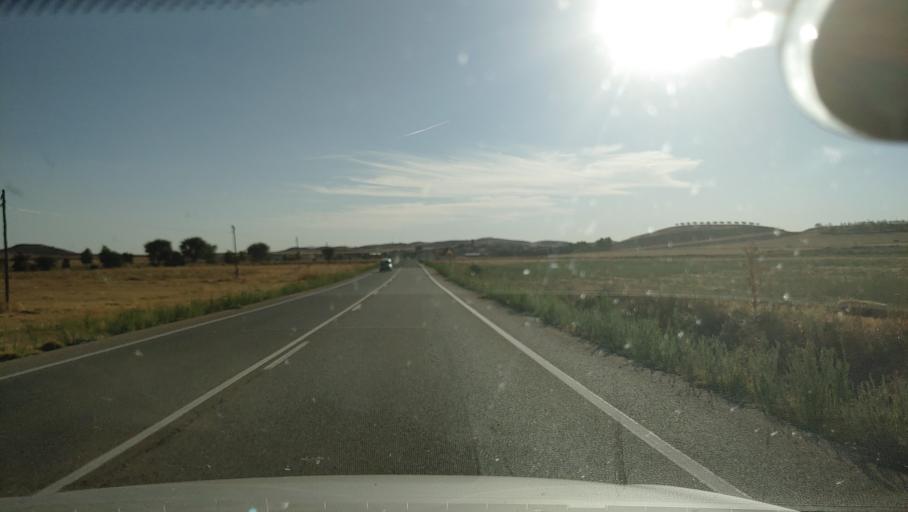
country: ES
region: Castille-La Mancha
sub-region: Provincia de Ciudad Real
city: Fuenllana
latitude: 38.7587
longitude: -2.9465
